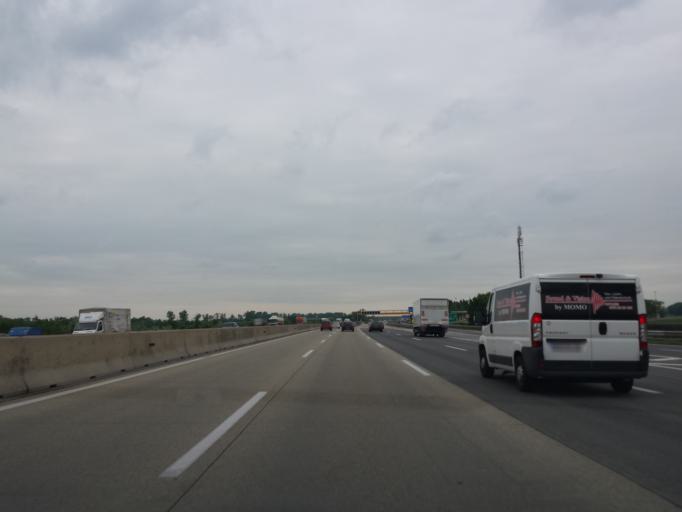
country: AT
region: Lower Austria
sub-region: Politischer Bezirk Modling
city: Guntramsdorf
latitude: 48.0373
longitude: 16.3404
